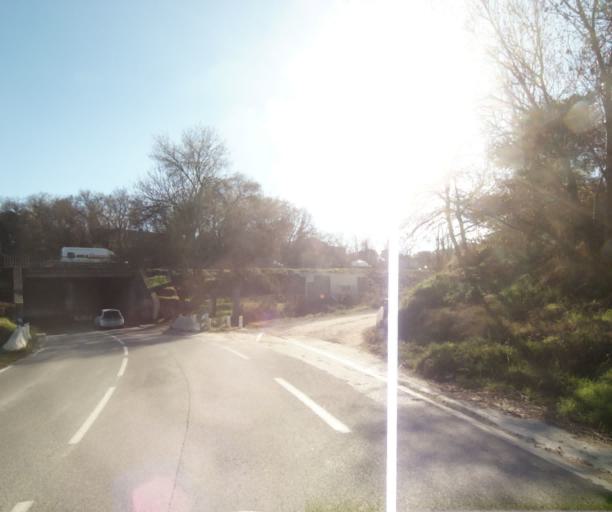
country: FR
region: Provence-Alpes-Cote d'Azur
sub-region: Departement des Alpes-Maritimes
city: Biot
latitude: 43.6122
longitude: 7.1085
